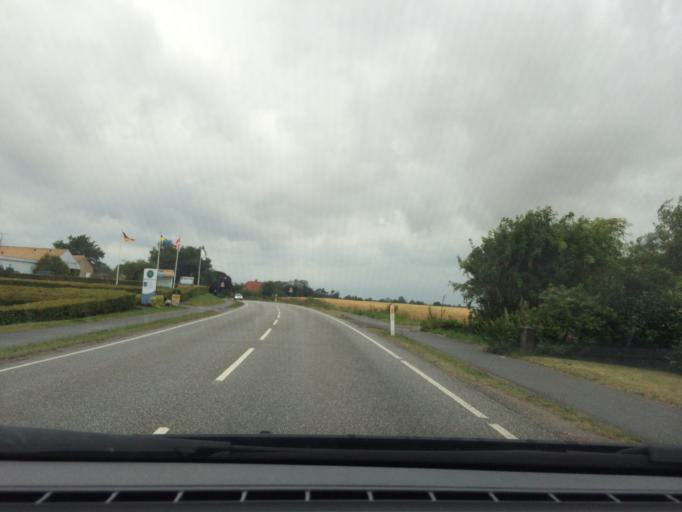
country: DK
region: Zealand
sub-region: Vordingborg Kommune
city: Stege
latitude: 54.9914
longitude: 12.3528
